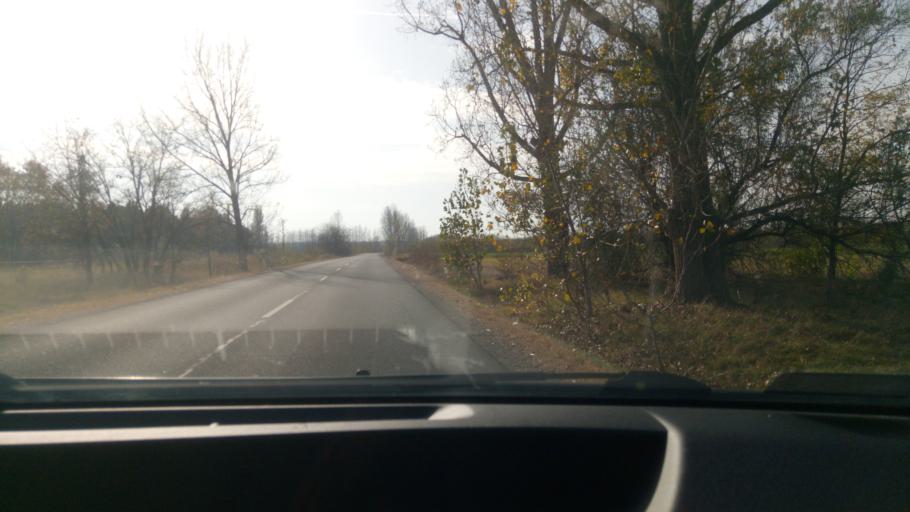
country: HU
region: Bacs-Kiskun
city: Jaszszentlaszlo
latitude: 46.6099
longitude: 19.7934
